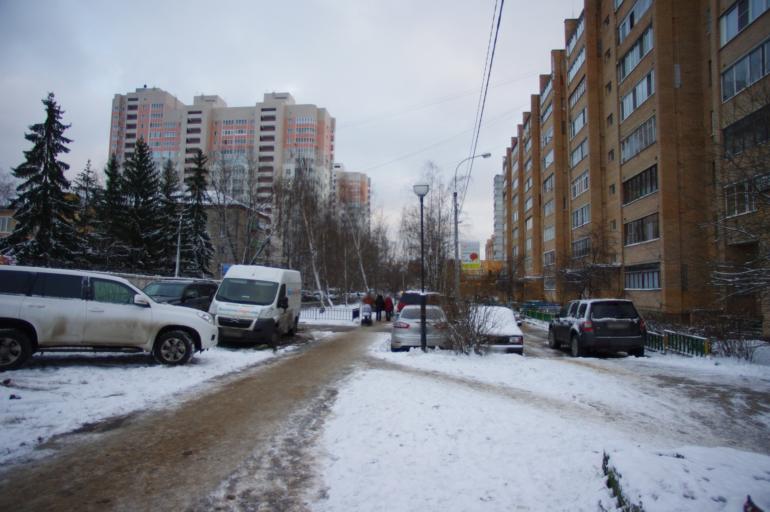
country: RU
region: Moskovskaya
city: Krasnogorsk
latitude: 55.8105
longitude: 37.3234
